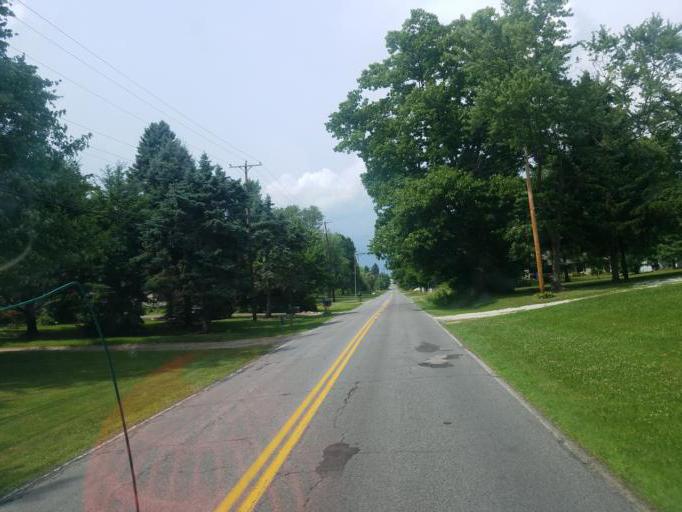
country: US
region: Ohio
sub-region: Portage County
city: Ravenna
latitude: 41.1007
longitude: -81.2204
